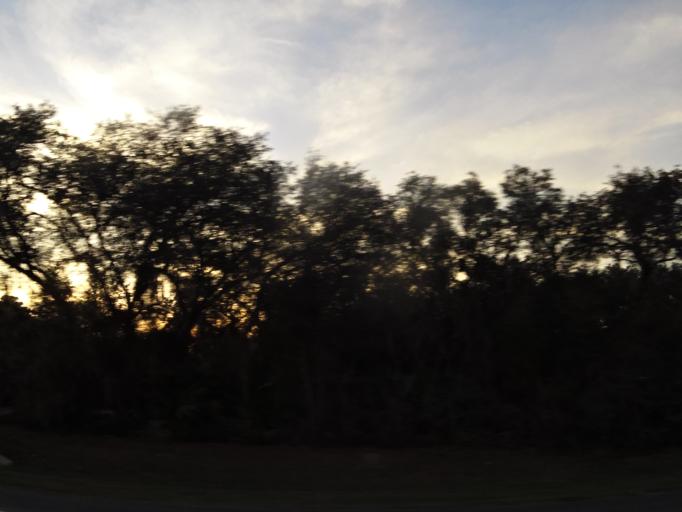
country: US
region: Florida
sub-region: Volusia County
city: North DeLand
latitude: 29.0986
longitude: -81.2957
